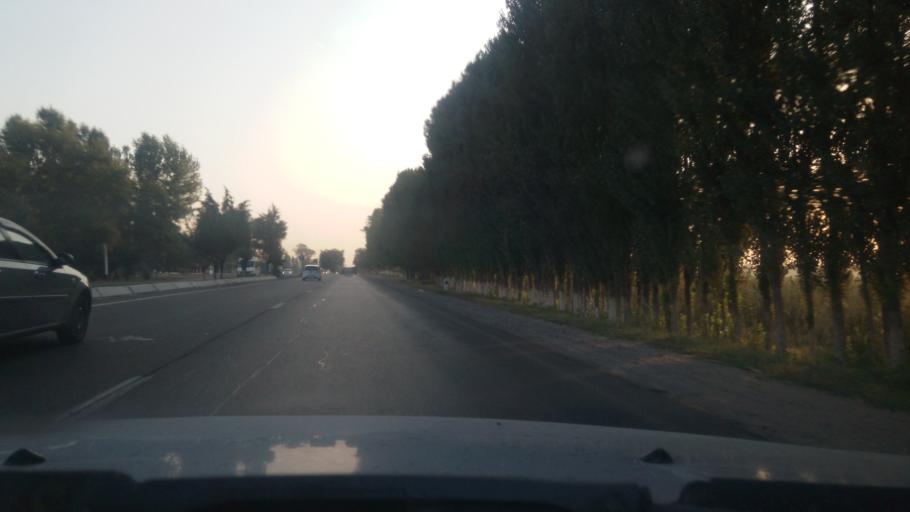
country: UZ
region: Toshkent
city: Yangiyul
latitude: 41.1716
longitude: 69.0667
